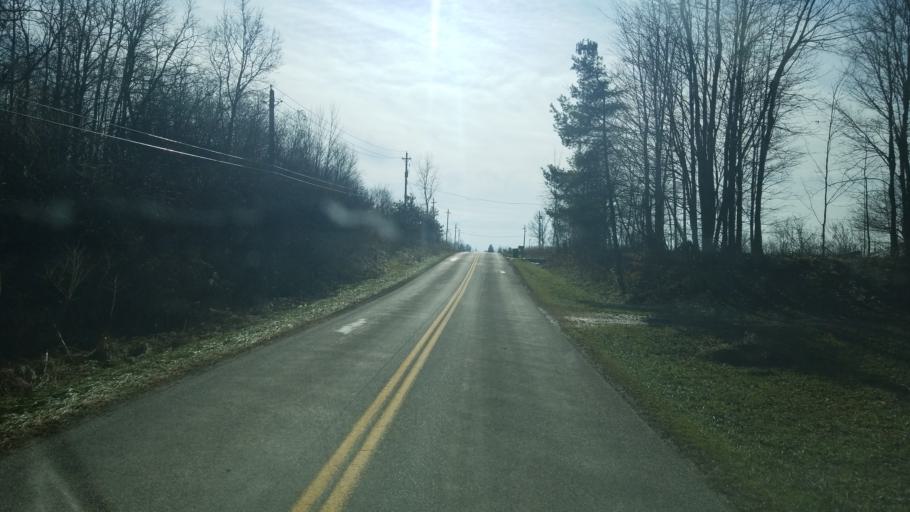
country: US
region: Ohio
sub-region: Ashtabula County
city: Roaming Shores
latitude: 41.6827
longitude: -80.8358
